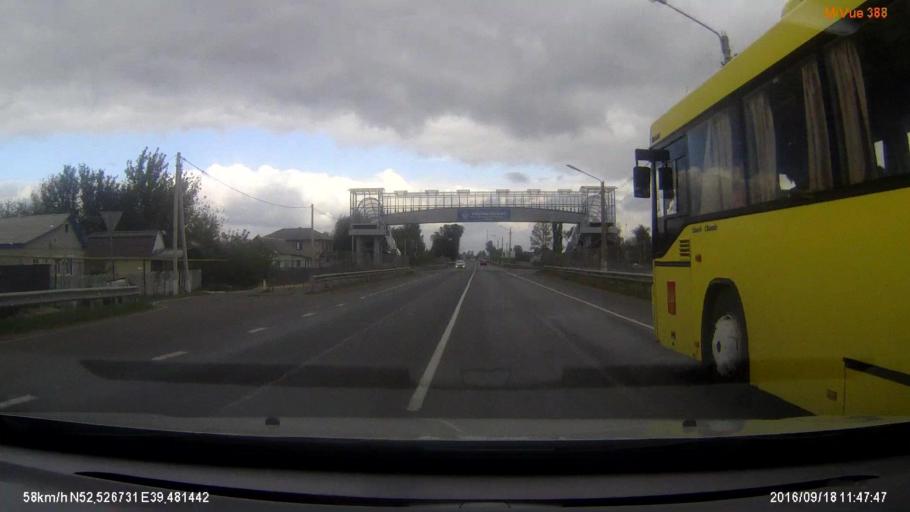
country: RU
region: Lipetsk
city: Syrskoye
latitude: 52.5266
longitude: 39.4812
